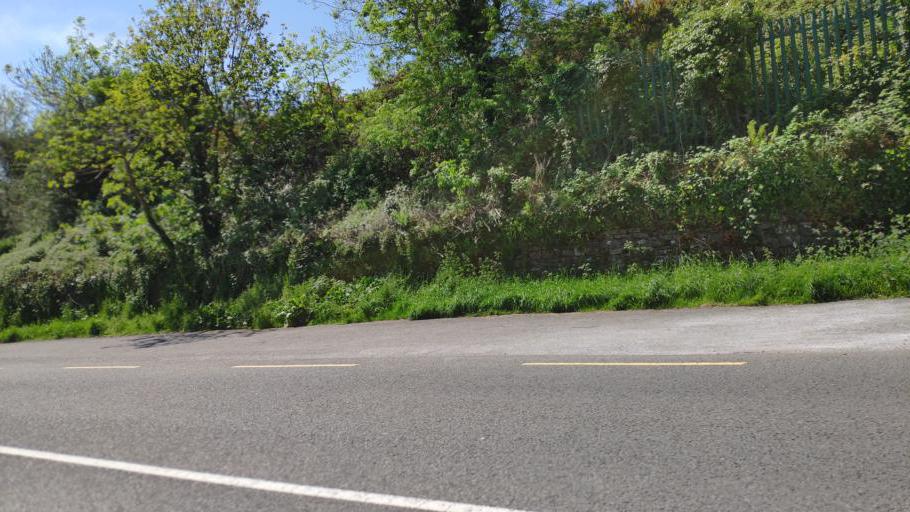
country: IE
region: Munster
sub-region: County Cork
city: Cork
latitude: 51.9283
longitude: -8.4880
